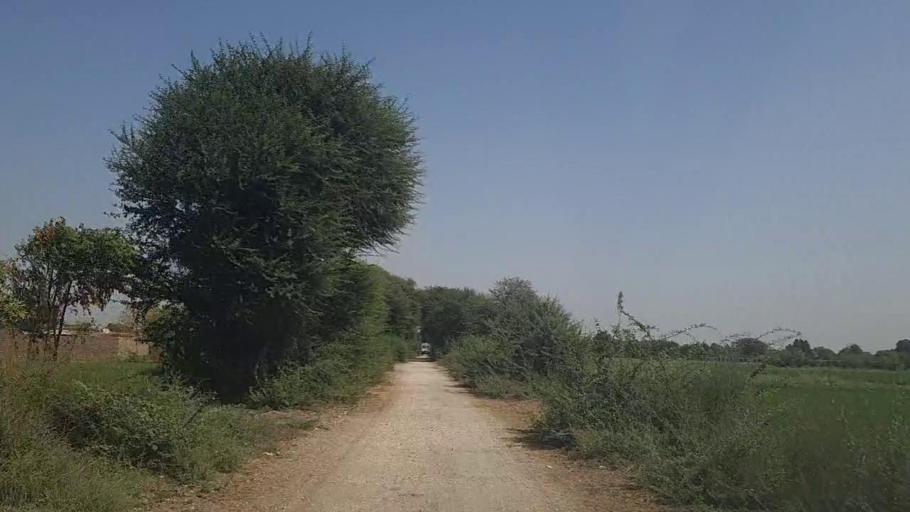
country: PK
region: Sindh
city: Naukot
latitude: 24.8406
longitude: 69.4139
